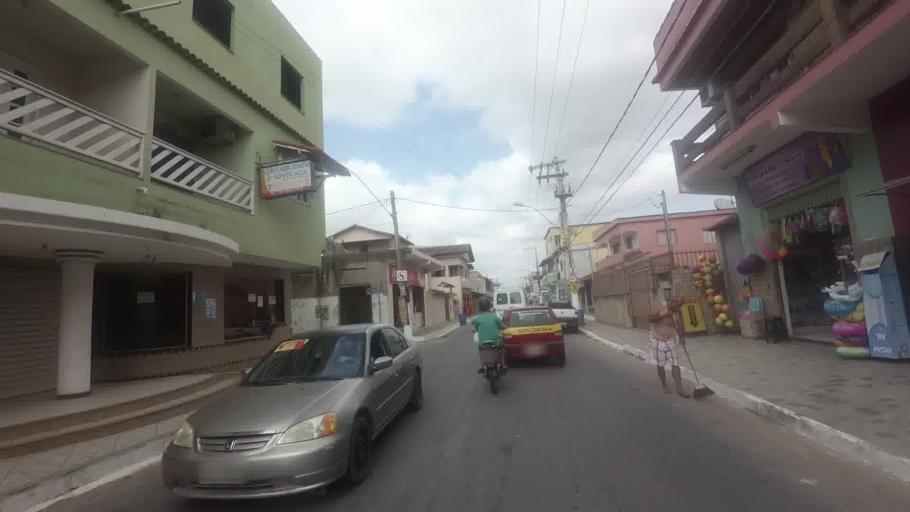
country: BR
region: Espirito Santo
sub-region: Piuma
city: Piuma
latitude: -20.9054
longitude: -40.7810
